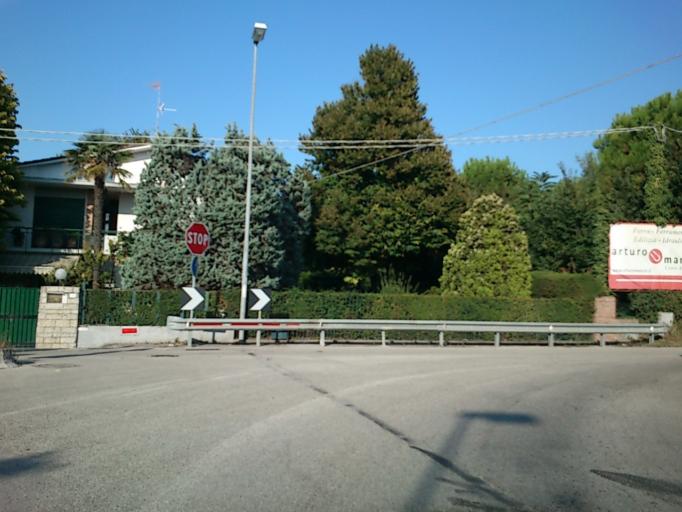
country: IT
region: The Marches
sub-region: Provincia di Pesaro e Urbino
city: Fano
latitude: 43.8273
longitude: 13.0423
